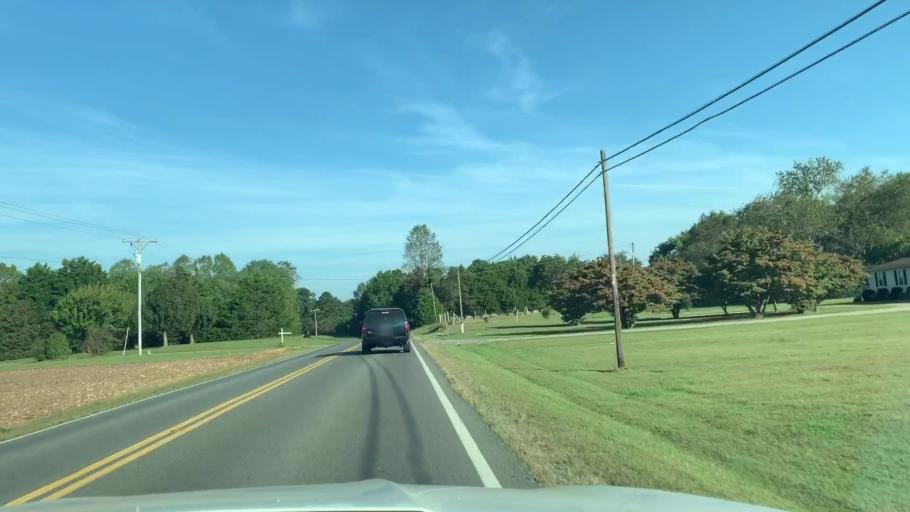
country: US
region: Virginia
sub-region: Lancaster County
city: Lancaster
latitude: 37.7605
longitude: -76.4214
